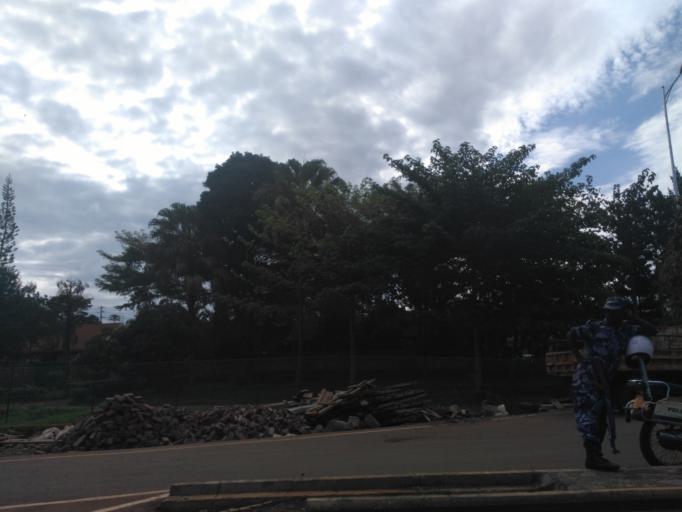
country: UG
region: Eastern Region
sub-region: Jinja District
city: Jinja
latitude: 0.4407
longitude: 33.1931
